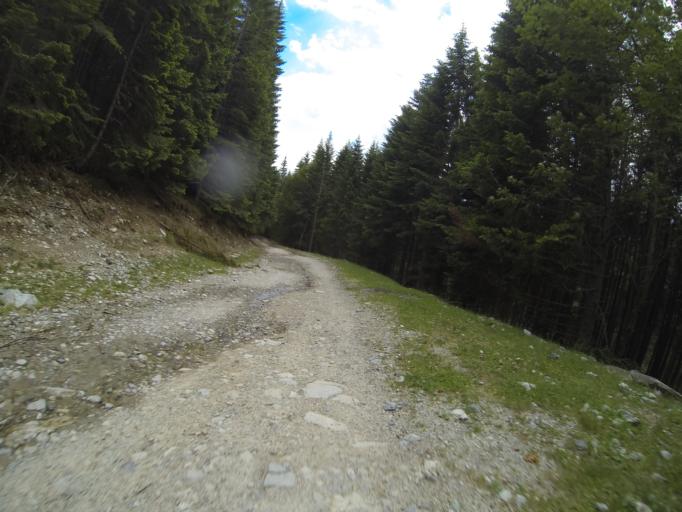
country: RO
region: Gorj
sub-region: Comuna Polovragi
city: Polovragi
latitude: 45.3383
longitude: 23.7942
